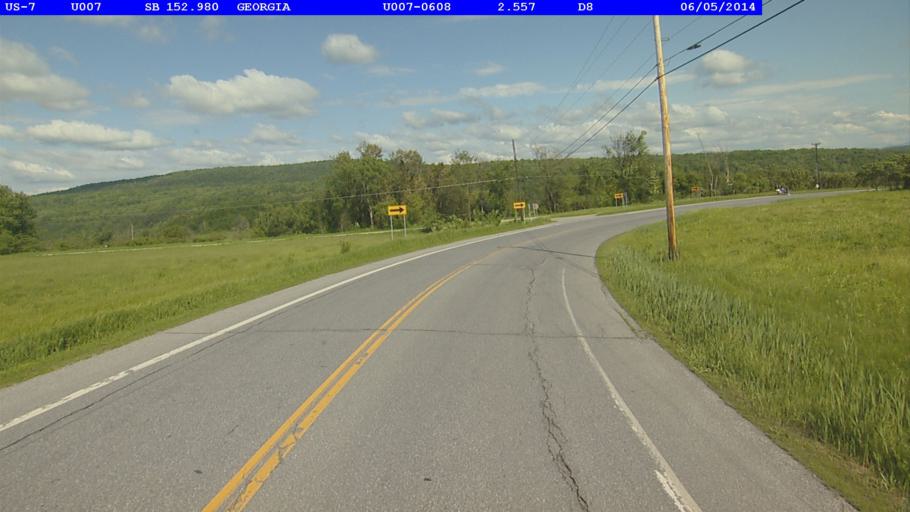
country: US
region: Vermont
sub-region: Chittenden County
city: Milton
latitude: 44.7149
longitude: -73.1024
